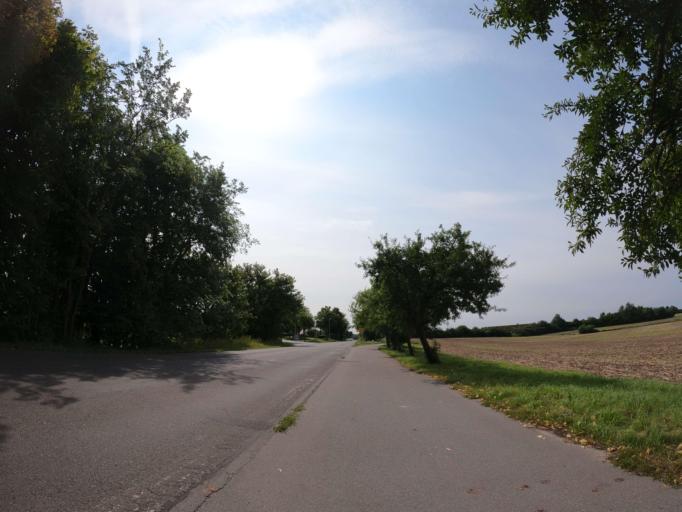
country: DE
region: Mecklenburg-Vorpommern
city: Kramerhof
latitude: 54.3445
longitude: 13.0686
